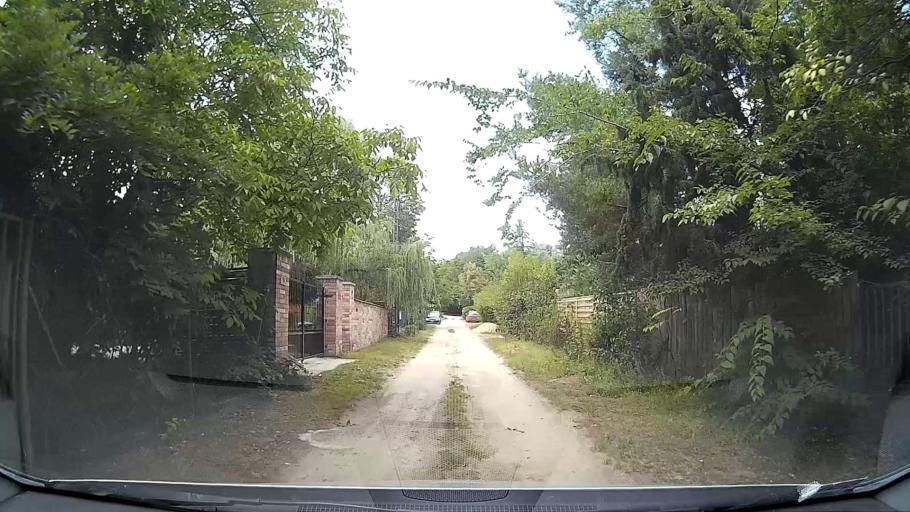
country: HU
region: Pest
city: Leanyfalu
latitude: 47.7183
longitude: 19.1142
